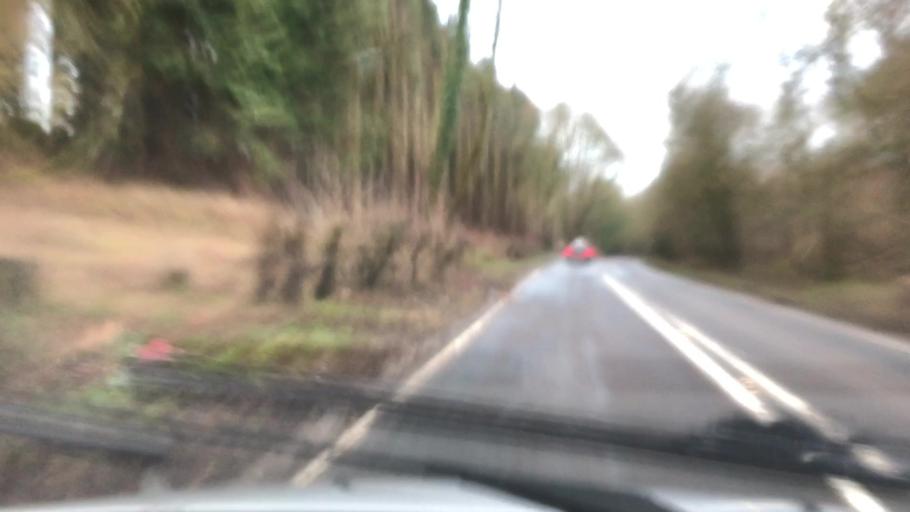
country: GB
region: England
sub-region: Hampshire
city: Alton
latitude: 51.1785
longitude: -0.9885
